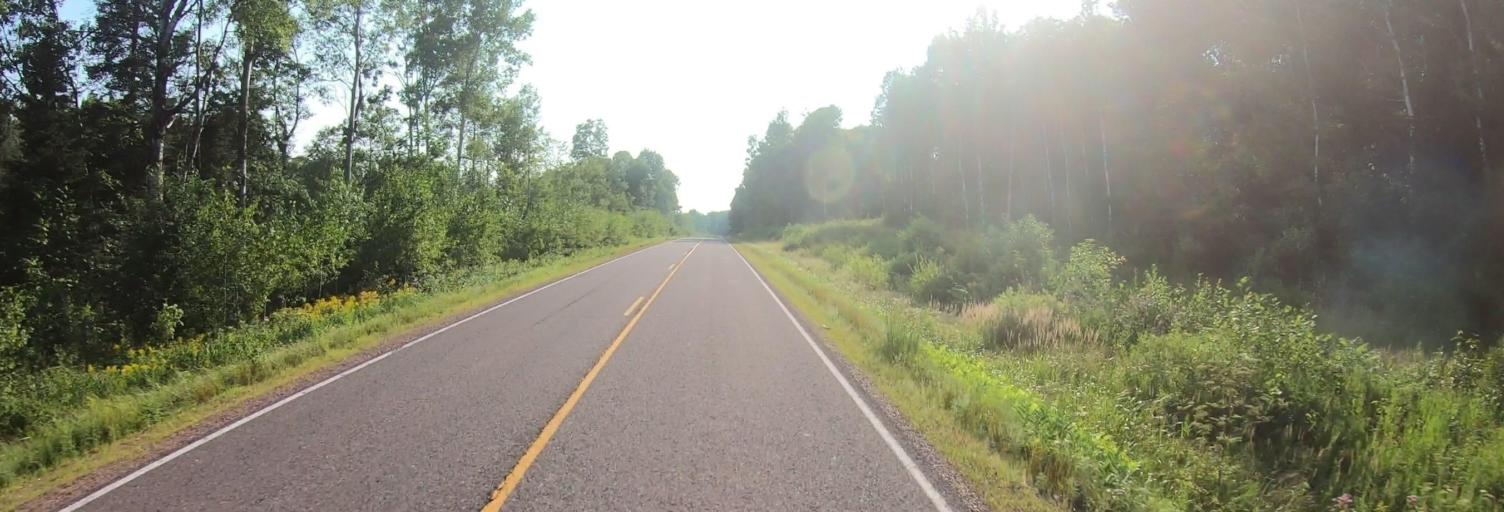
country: US
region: Wisconsin
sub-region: Ashland County
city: Ashland
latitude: 46.3151
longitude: -90.6915
